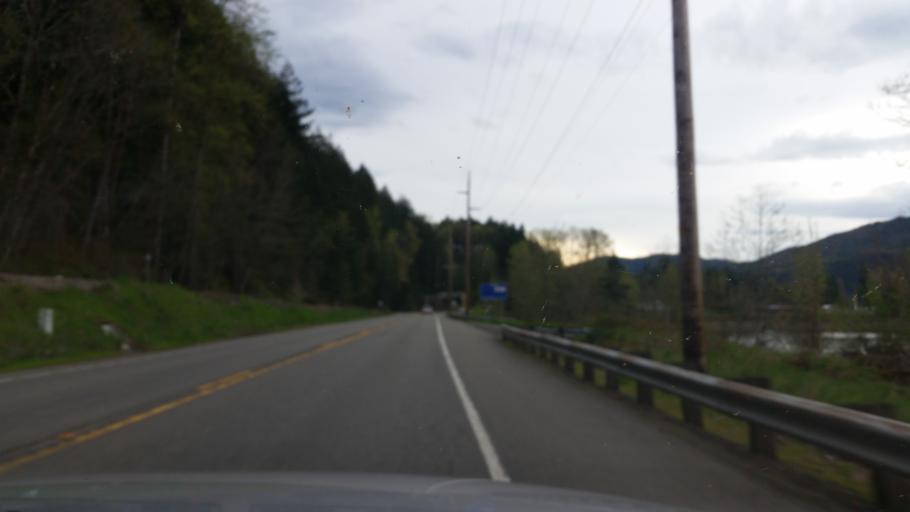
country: US
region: Washington
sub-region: Pierce County
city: Eatonville
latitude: 46.7688
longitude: -122.2009
